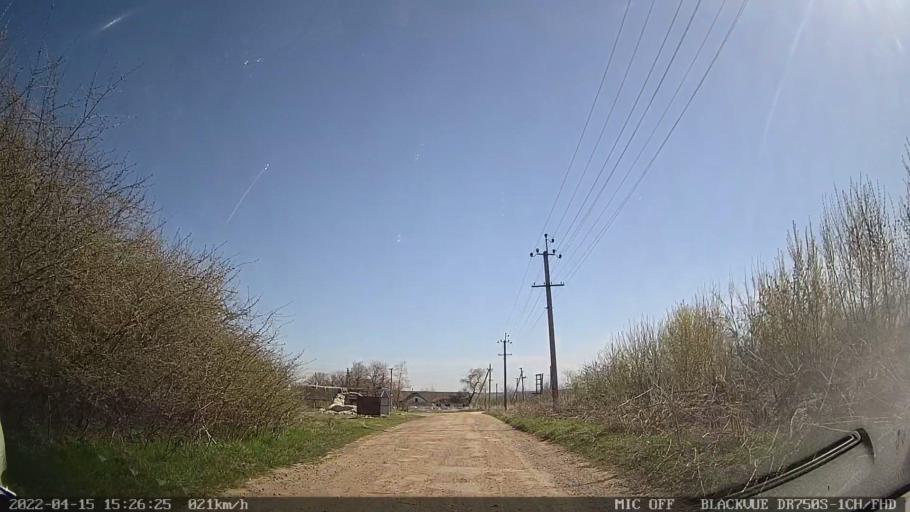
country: MD
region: Raionul Ocnita
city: Otaci
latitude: 48.3623
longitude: 27.9284
